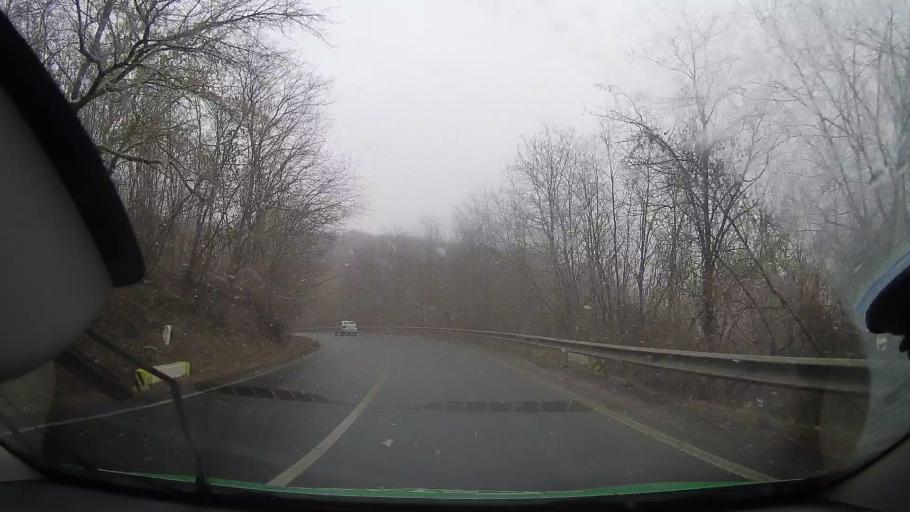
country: RO
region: Sibiu
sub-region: Municipiul Medias
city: Medias
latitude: 46.1807
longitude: 24.3350
